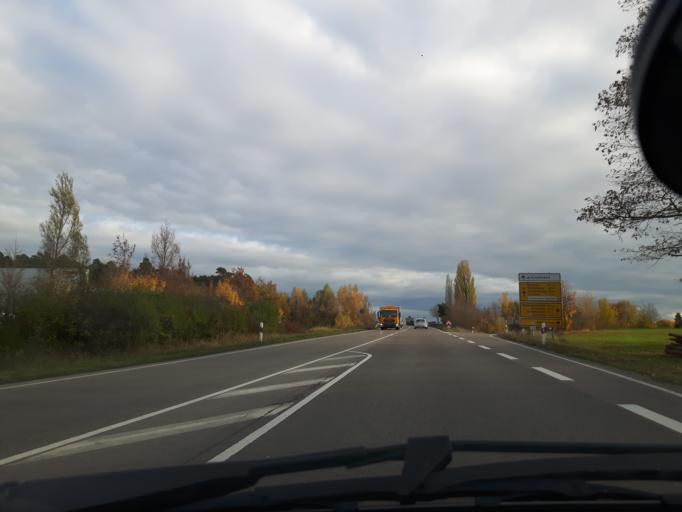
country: DE
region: Bavaria
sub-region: Regierungsbezirk Mittelfranken
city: Burgoberbach
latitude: 49.2531
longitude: 10.5912
